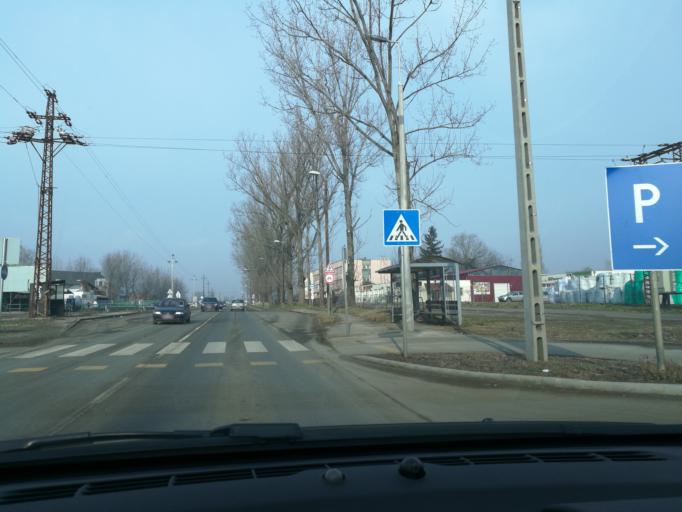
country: HU
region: Szabolcs-Szatmar-Bereg
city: Nyiregyhaza
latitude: 47.9656
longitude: 21.6982
